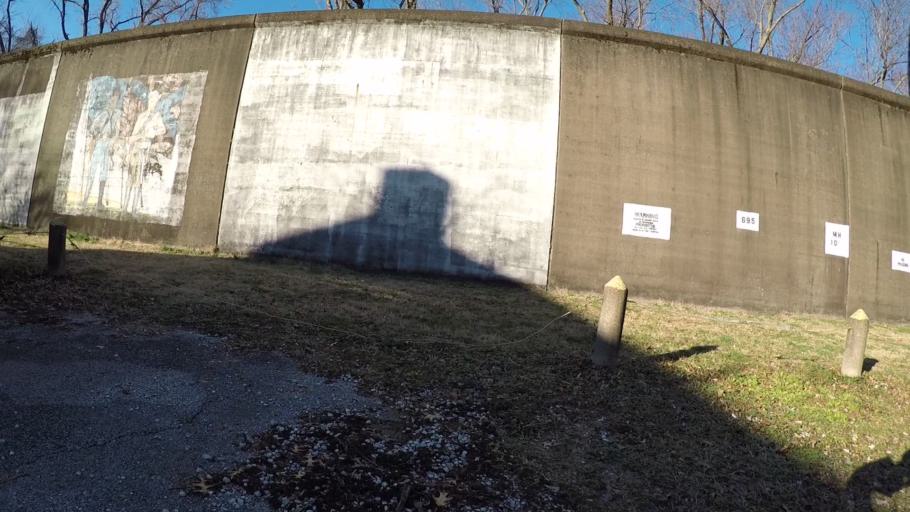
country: US
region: West Virginia
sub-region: Cabell County
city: Huntington
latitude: 38.4304
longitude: -82.3823
